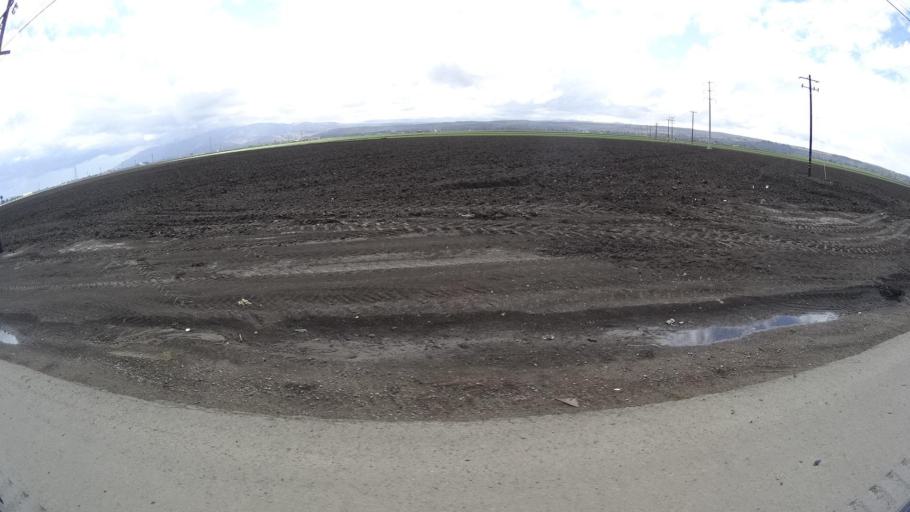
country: US
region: California
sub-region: Monterey County
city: Boronda
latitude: 36.6786
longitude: -121.7077
